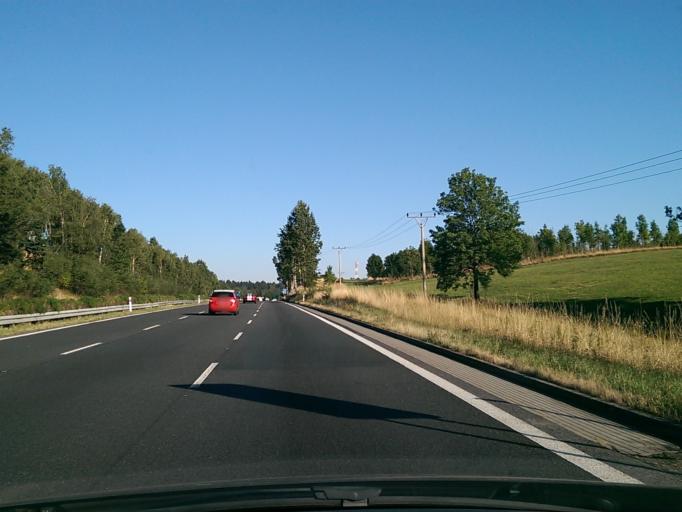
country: CZ
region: Liberecky
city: Hodkovice nad Mohelkou
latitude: 50.7107
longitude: 15.0827
